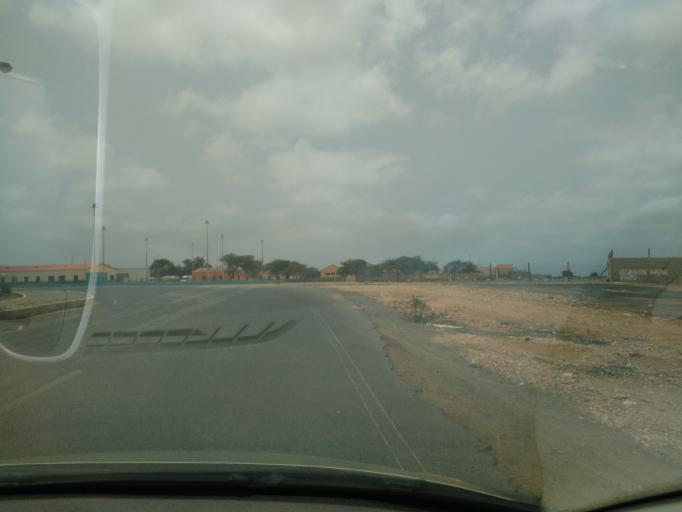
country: CV
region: Sal
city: Espargos
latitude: 16.7528
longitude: -22.9466
